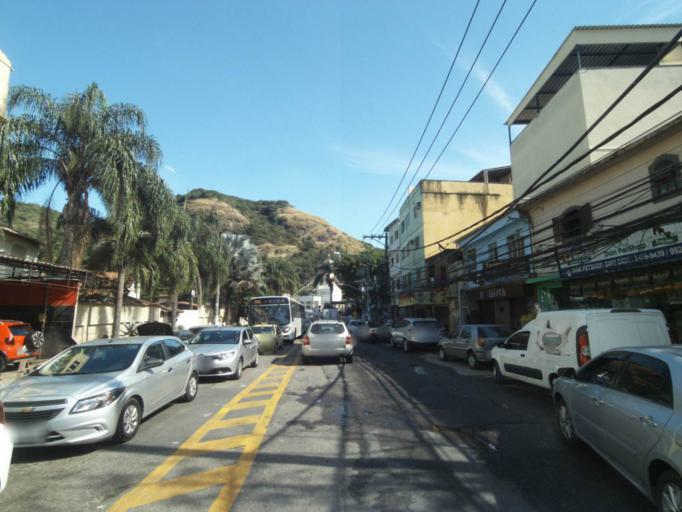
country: BR
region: Rio de Janeiro
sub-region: Rio De Janeiro
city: Rio de Janeiro
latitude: -22.9878
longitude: -43.3100
